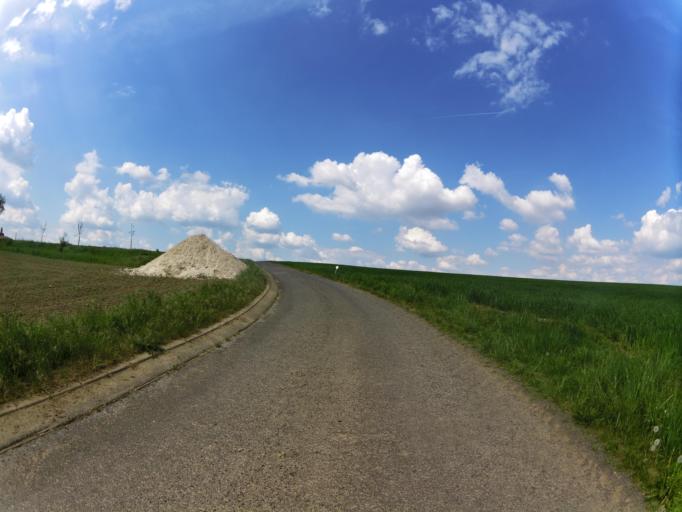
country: DE
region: Bavaria
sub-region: Regierungsbezirk Unterfranken
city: Giebelstadt
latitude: 49.6250
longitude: 9.9277
